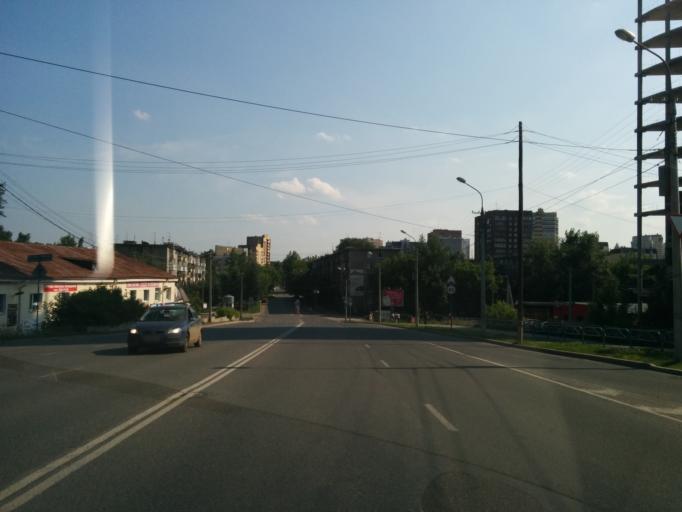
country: RU
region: Perm
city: Perm
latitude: 58.0024
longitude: 56.2075
